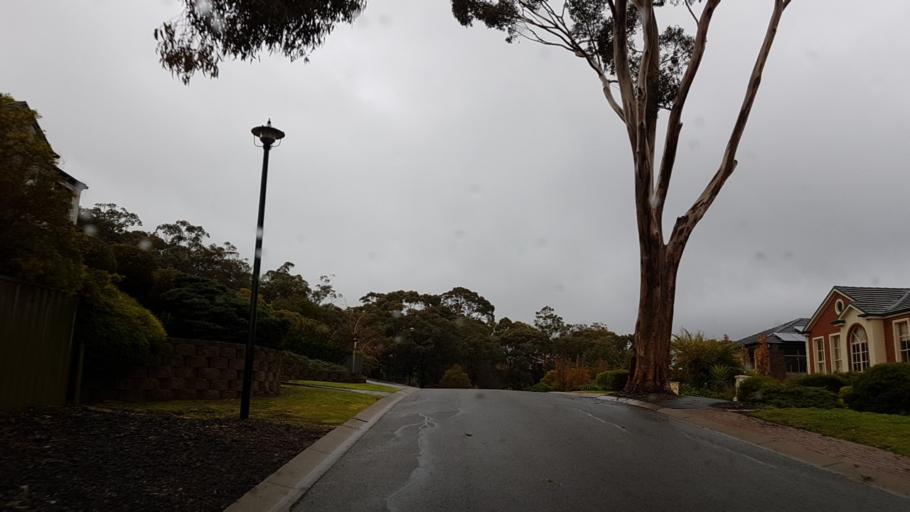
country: AU
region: South Australia
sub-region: Onkaparinga
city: Craigburn Farm
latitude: -35.0864
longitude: 138.5965
